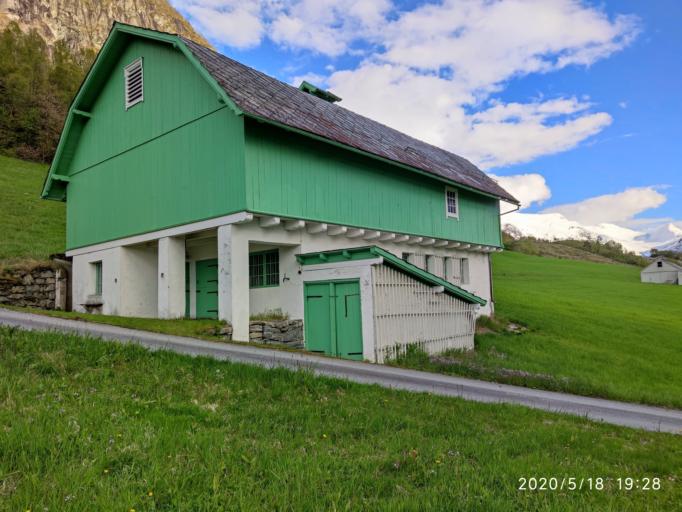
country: NO
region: Sogn og Fjordane
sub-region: Stryn
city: Stryn
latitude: 61.8324
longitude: 6.8139
